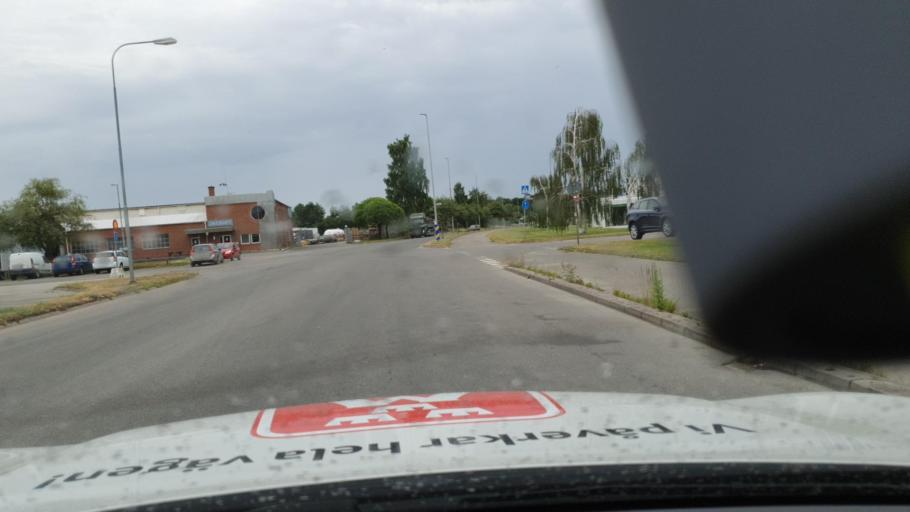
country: SE
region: Vaestra Goetaland
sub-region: Hjo Kommun
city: Hjo
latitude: 58.3103
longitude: 14.2911
